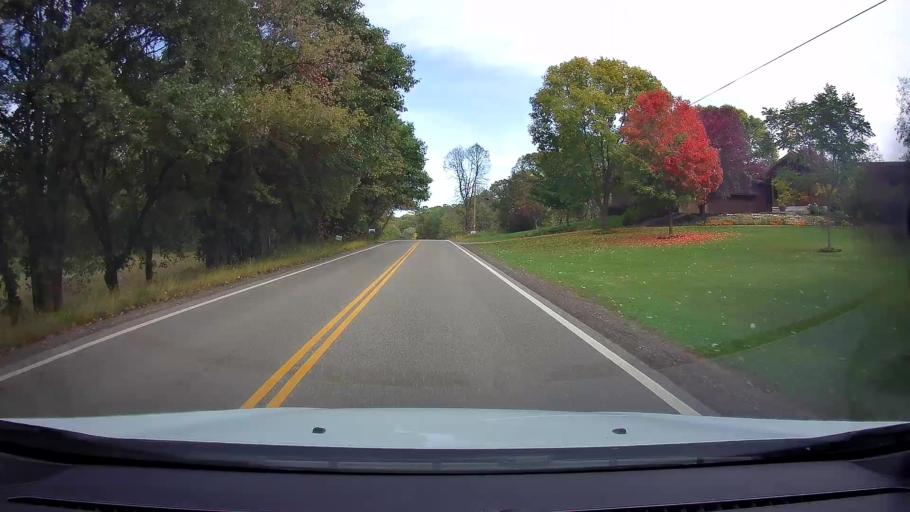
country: US
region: Minnesota
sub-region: Washington County
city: Stillwater
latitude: 45.0894
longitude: -92.8240
